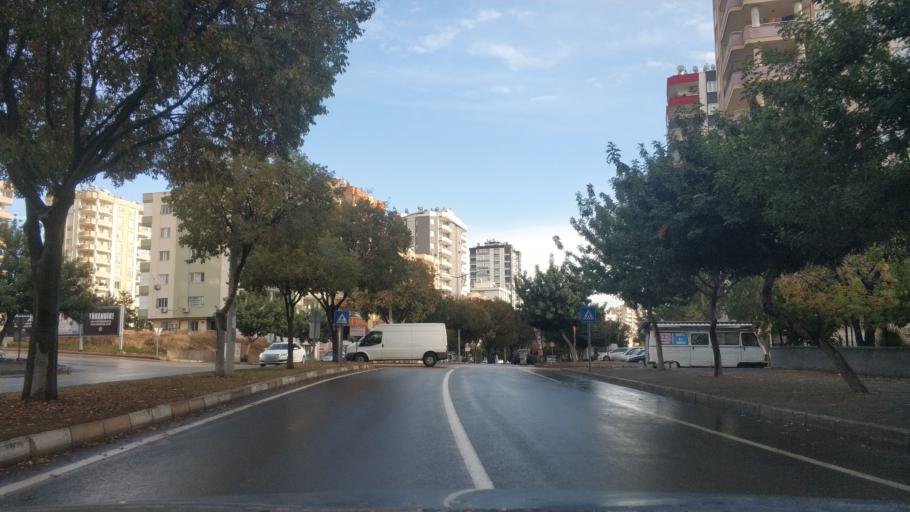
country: TR
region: Adana
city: Seyhan
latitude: 37.0398
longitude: 35.2753
